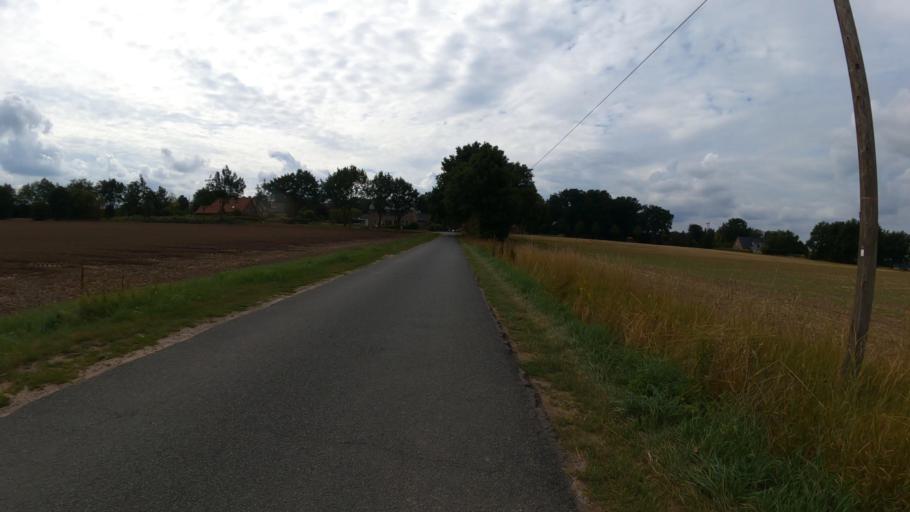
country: DE
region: Lower Saxony
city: Appel
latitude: 53.3991
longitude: 9.7795
